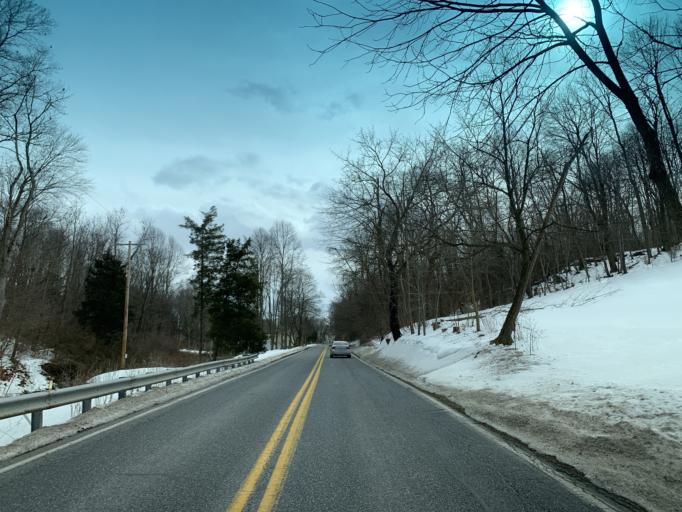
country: US
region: Pennsylvania
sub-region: York County
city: Shrewsbury
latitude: 39.8119
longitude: -76.6294
